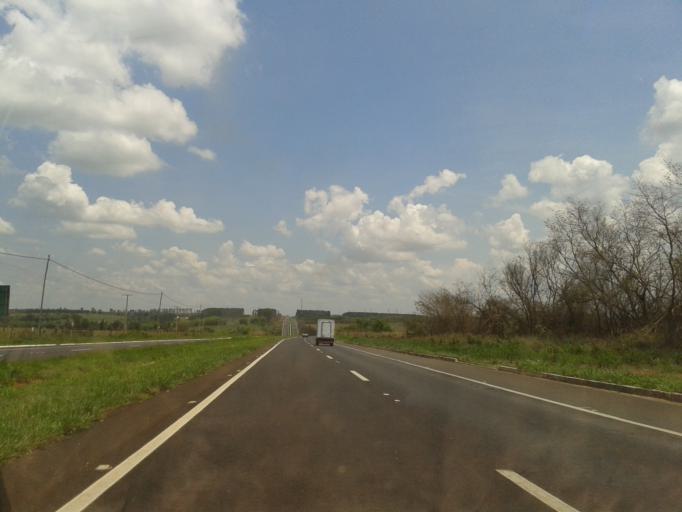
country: BR
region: Minas Gerais
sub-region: Uberlandia
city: Uberlandia
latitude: -18.8855
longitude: -48.4644
